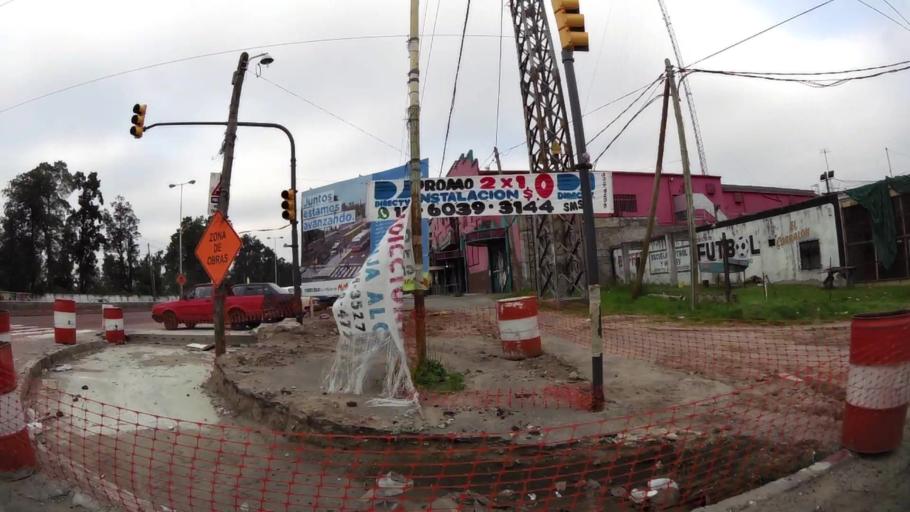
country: AR
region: Buenos Aires
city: San Justo
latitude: -34.7012
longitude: -58.5797
